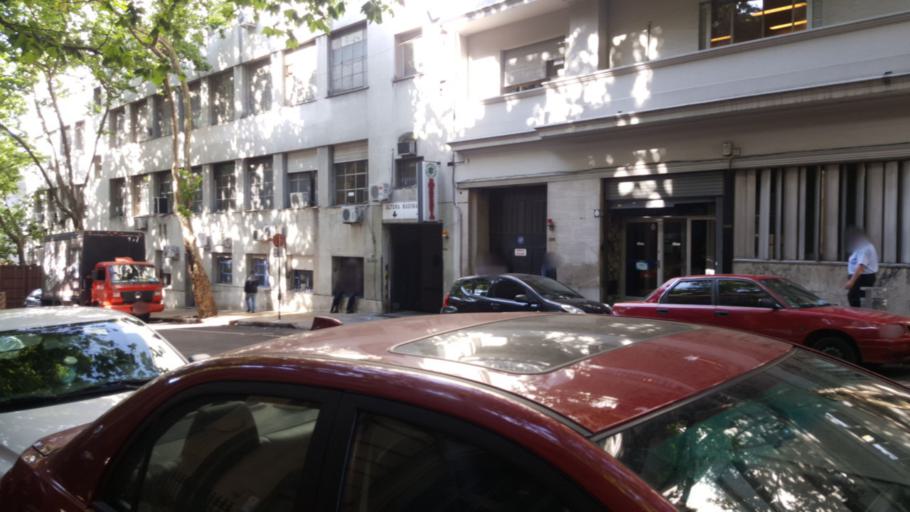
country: UY
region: Montevideo
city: Montevideo
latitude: -34.9047
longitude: -56.1947
